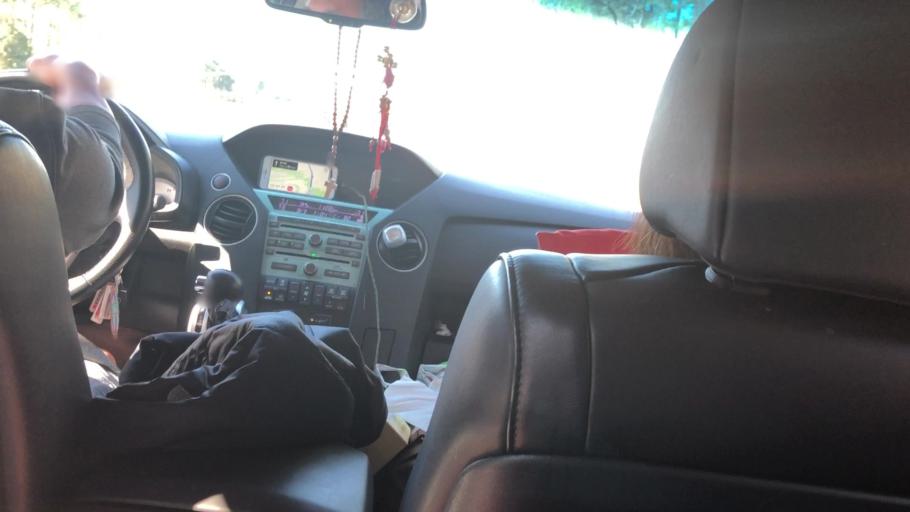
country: US
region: Louisiana
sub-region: Saint John the Baptist Parish
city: Montegut
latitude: 30.1031
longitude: -90.4897
